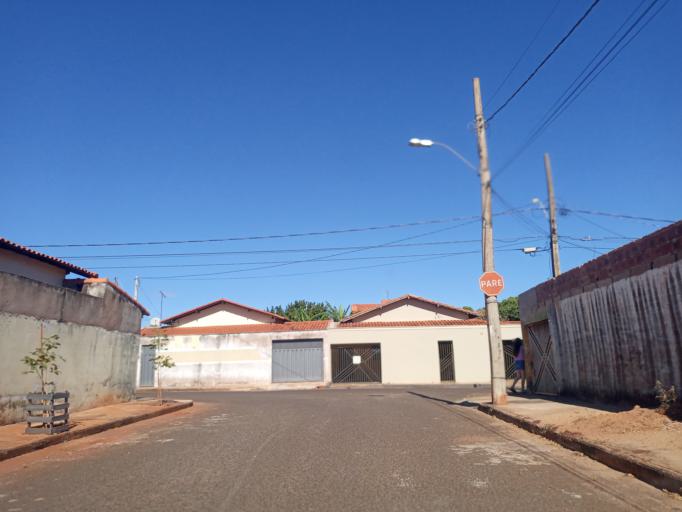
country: BR
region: Minas Gerais
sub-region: Ituiutaba
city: Ituiutaba
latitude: -18.9670
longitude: -49.4473
